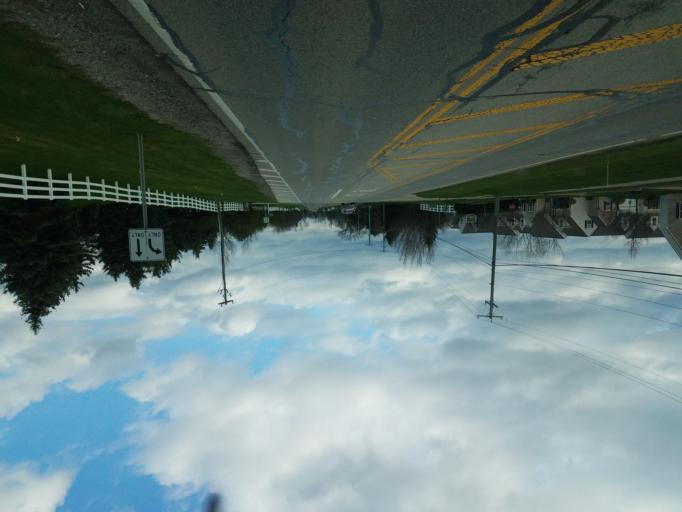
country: US
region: Ohio
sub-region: Delaware County
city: Powell
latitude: 40.1724
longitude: -83.0775
